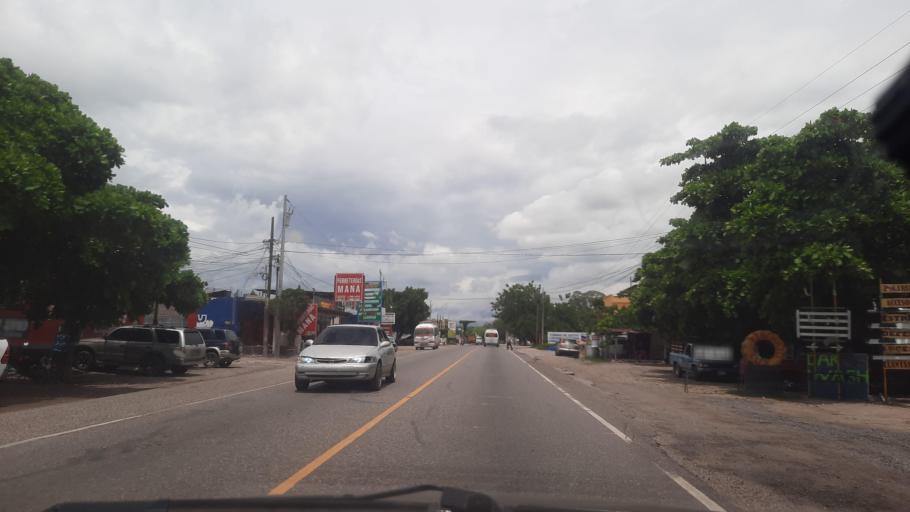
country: GT
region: Zacapa
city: Estanzuela
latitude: 14.9972
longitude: -89.5675
